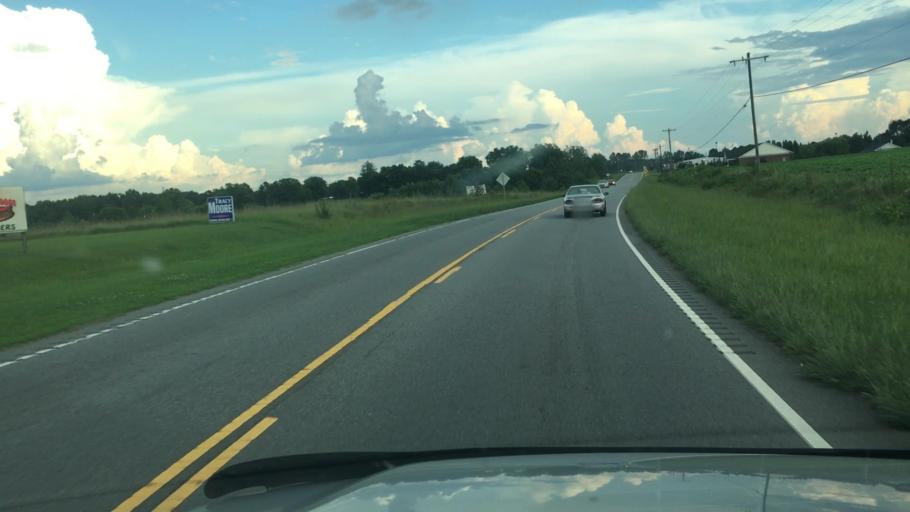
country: US
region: South Carolina
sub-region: Cherokee County
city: Gaffney
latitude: 35.1108
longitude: -81.6997
